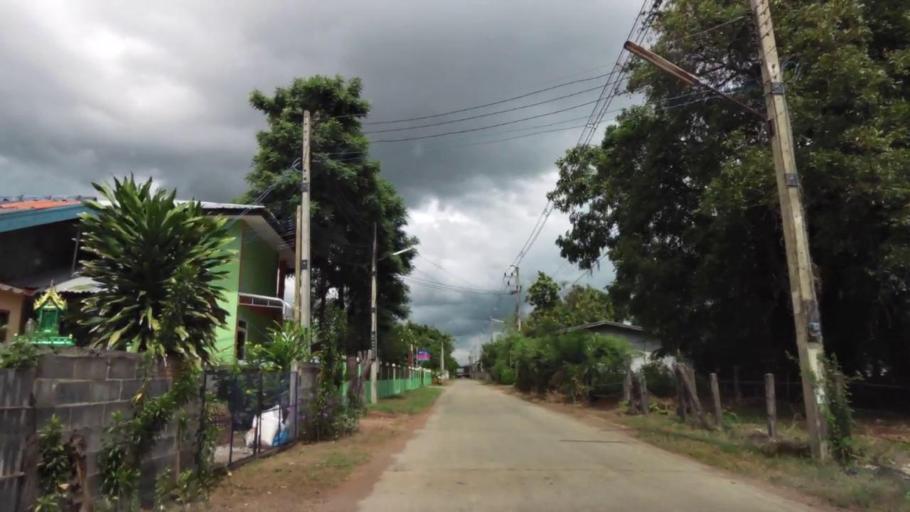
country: TH
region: Nakhon Sawan
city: Phai Sali
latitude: 15.5957
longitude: 100.6492
